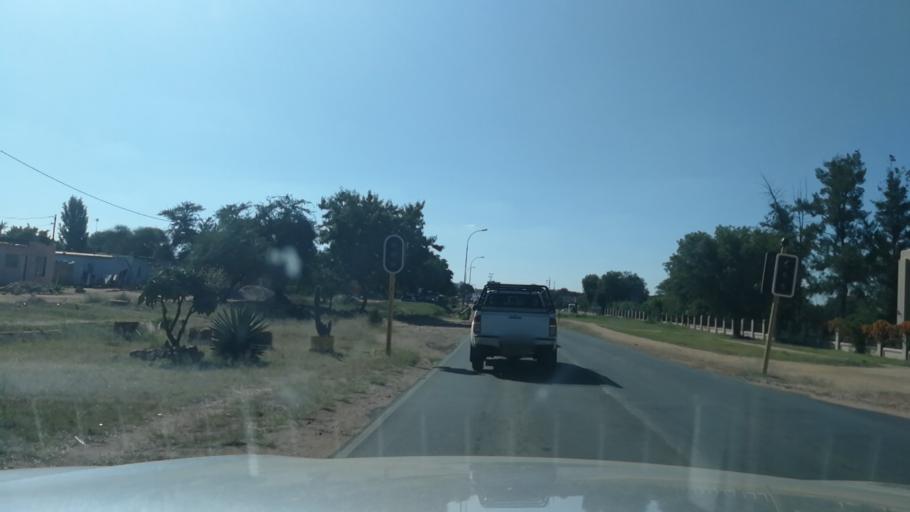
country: BW
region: South East
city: Gaborone
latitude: -24.6840
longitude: 25.9057
